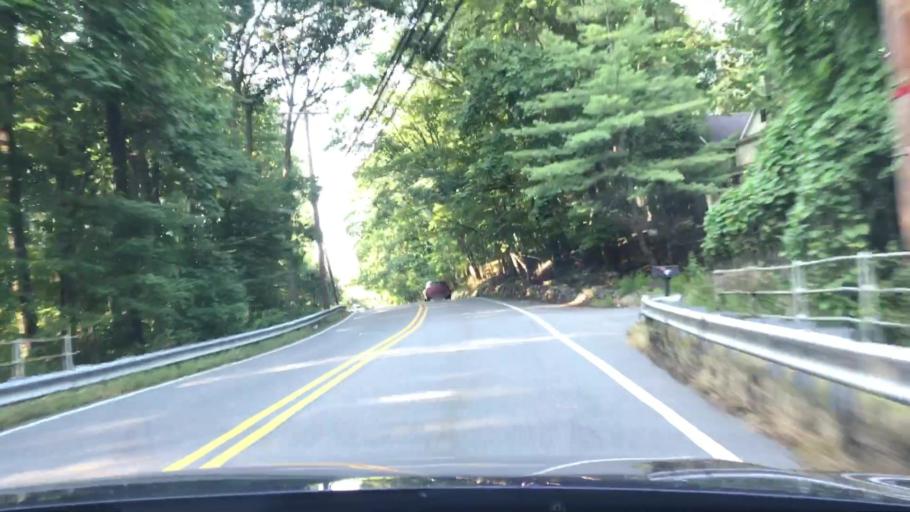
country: US
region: New Jersey
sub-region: Bergen County
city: Northvale
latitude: 40.9895
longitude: -73.9351
